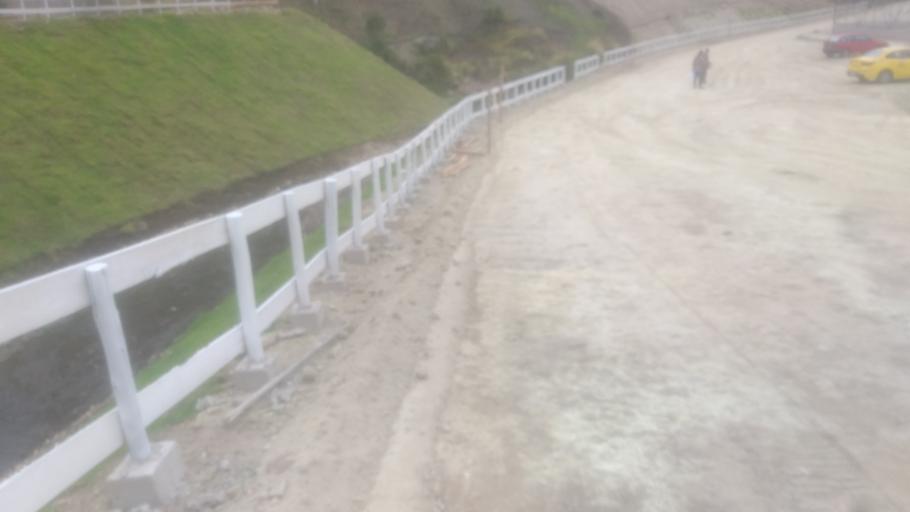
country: EC
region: Chimborazo
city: Riobamba
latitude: -1.7087
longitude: -78.7040
